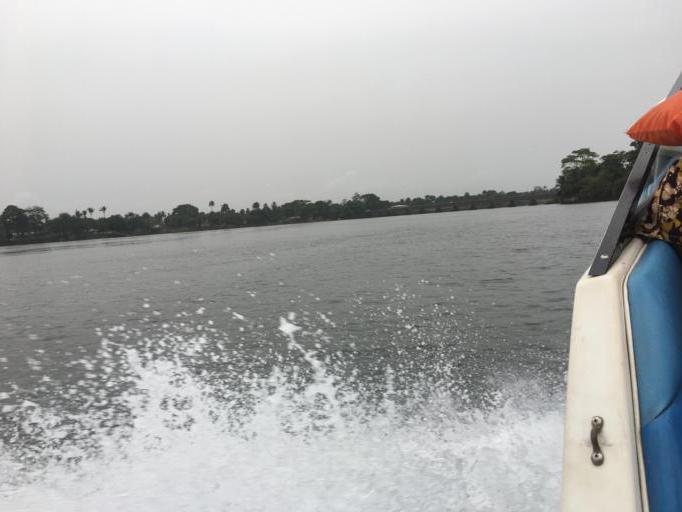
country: LR
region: Montserrado
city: Monrovia
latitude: 6.3911
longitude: -10.7864
